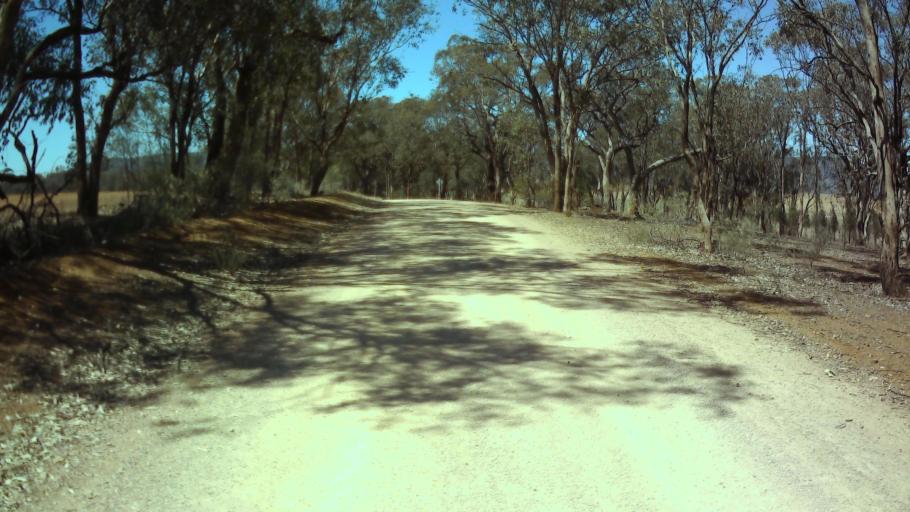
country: AU
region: New South Wales
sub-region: Weddin
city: Grenfell
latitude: -33.9322
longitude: 148.0773
